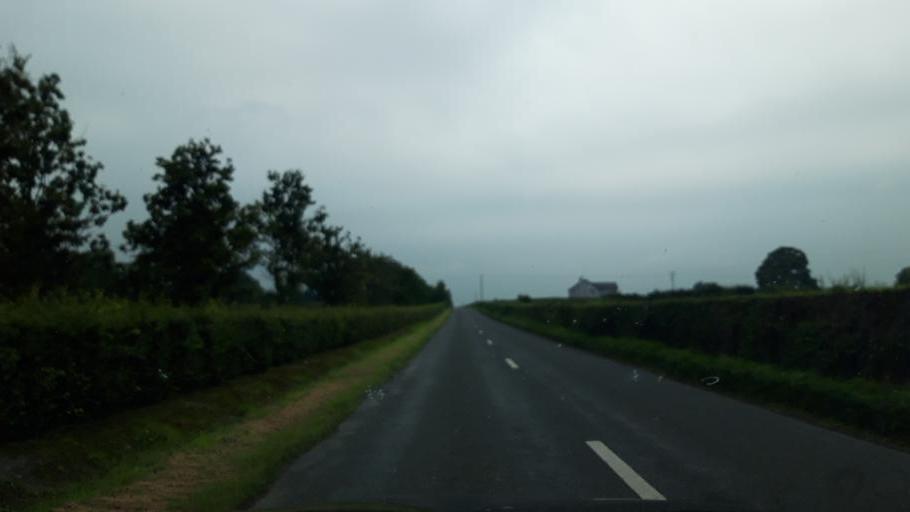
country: IE
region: Munster
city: Fethard
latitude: 52.4887
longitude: -7.6919
